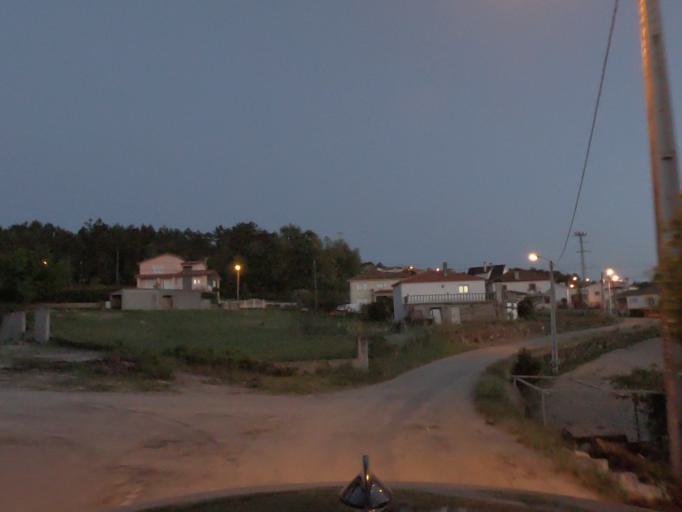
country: PT
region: Vila Real
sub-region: Vila Real
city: Vila Real
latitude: 41.3244
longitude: -7.6871
